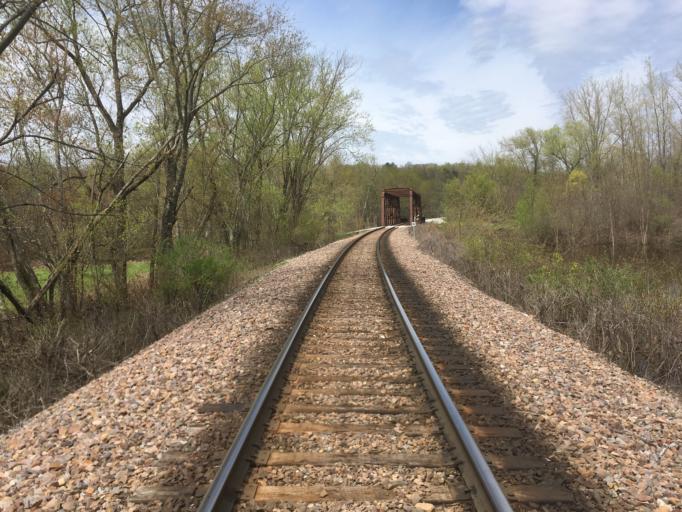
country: US
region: Vermont
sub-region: Rutland County
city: Brandon
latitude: 43.7164
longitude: -73.0502
